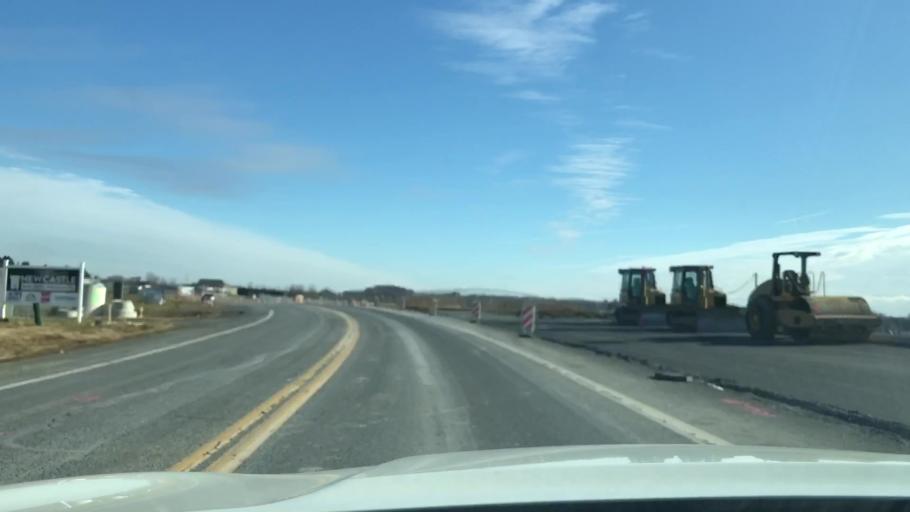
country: US
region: Pennsylvania
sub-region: Lehigh County
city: Catasauqua
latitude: 40.6617
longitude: -75.4308
